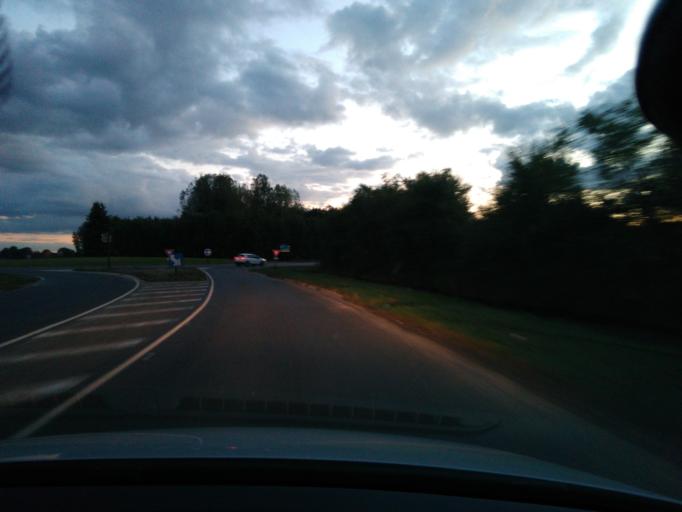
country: FR
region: Ile-de-France
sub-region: Departement de Seine-et-Marne
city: Villeneuve-le-Comte
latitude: 48.8243
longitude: 2.8353
